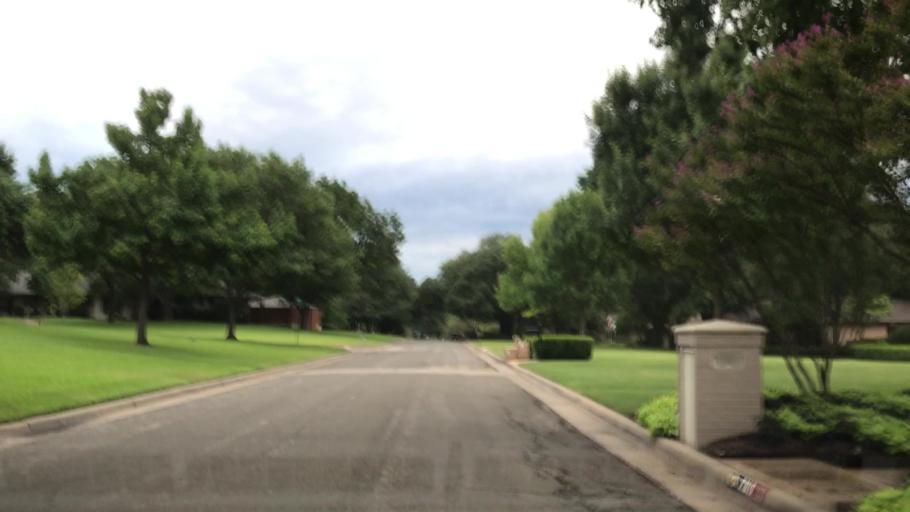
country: US
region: Texas
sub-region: Dallas County
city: Addison
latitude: 32.9342
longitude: -96.7827
